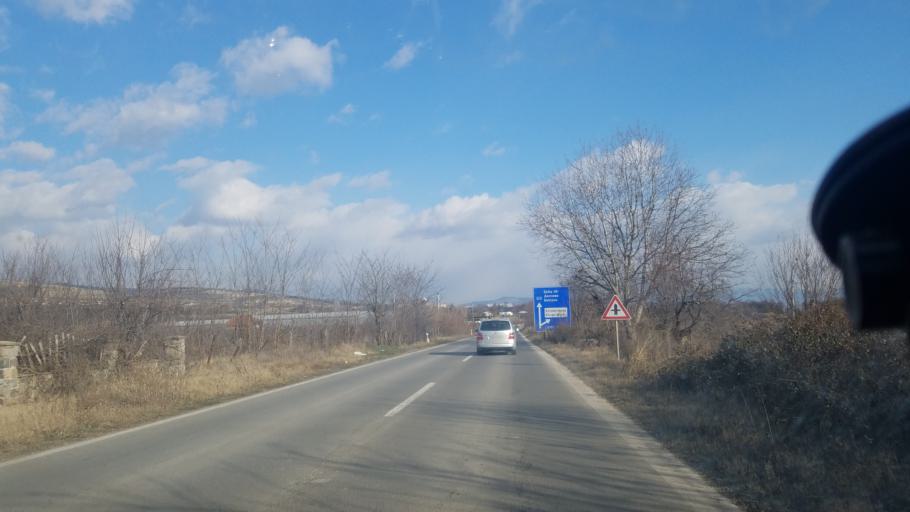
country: MK
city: Obleshevo
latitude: 41.8988
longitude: 22.3686
